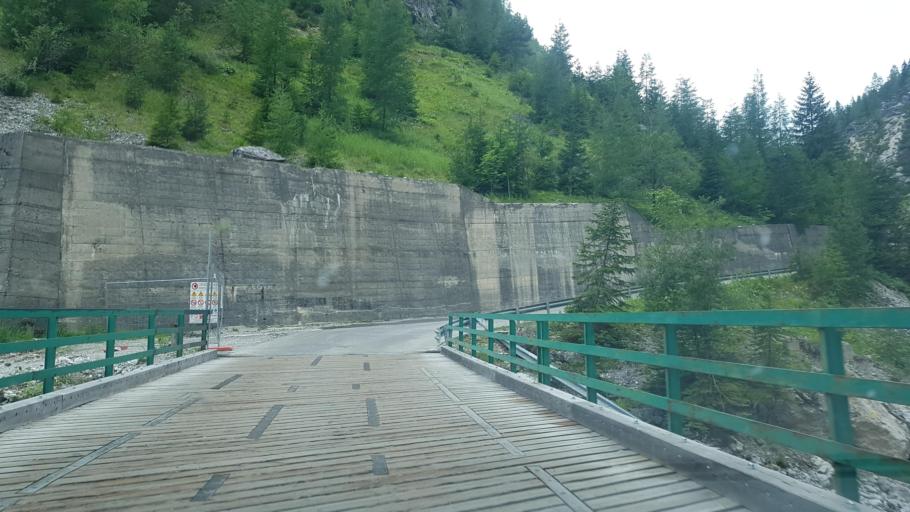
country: IT
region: Veneto
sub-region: Provincia di Belluno
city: San Pietro di Cadore
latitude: 46.5932
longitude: 12.6312
